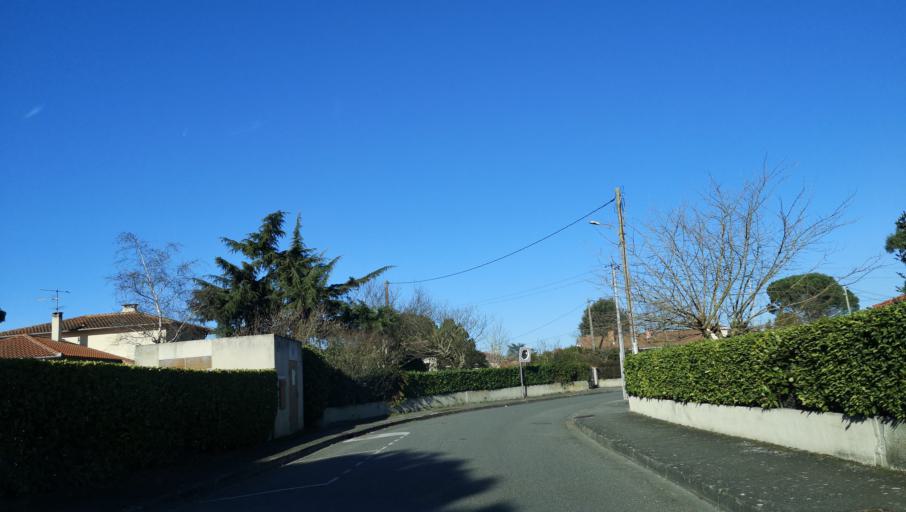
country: FR
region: Midi-Pyrenees
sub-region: Departement de la Haute-Garonne
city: Beauzelle
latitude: 43.6632
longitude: 1.3833
